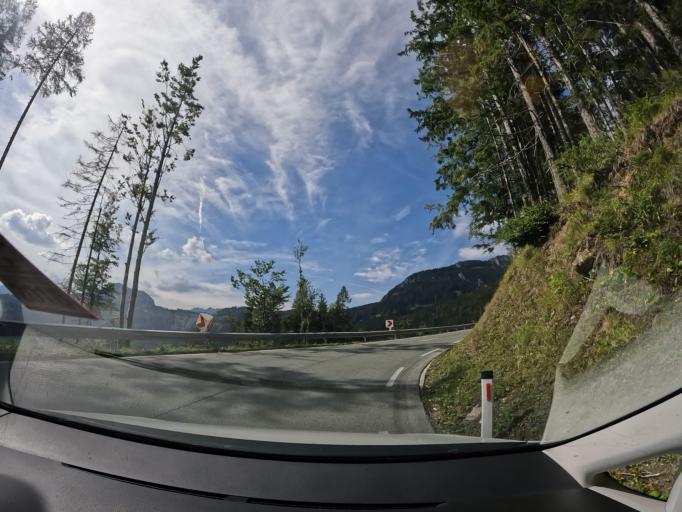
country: AT
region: Carinthia
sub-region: Politischer Bezirk Sankt Veit an der Glan
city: Liebenfels
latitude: 46.7037
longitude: 14.2947
